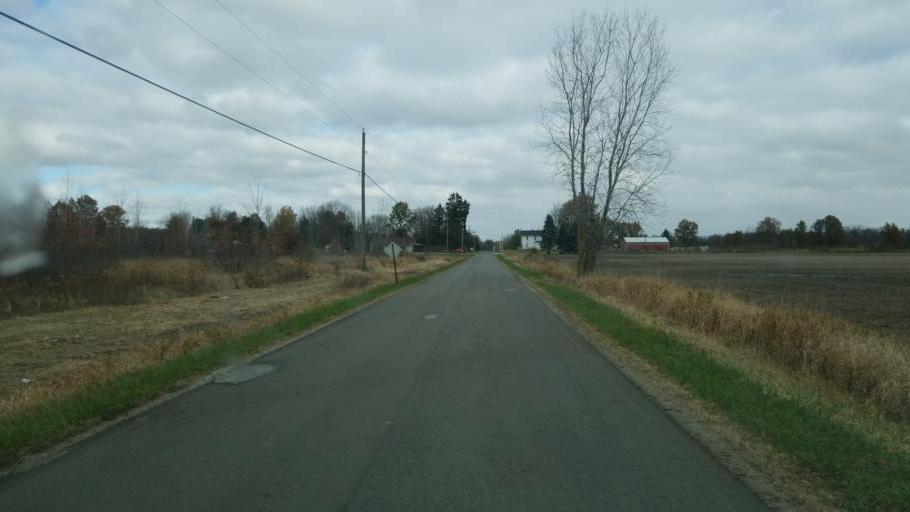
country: US
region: Ohio
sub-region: Crawford County
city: Galion
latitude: 40.7003
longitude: -82.7933
